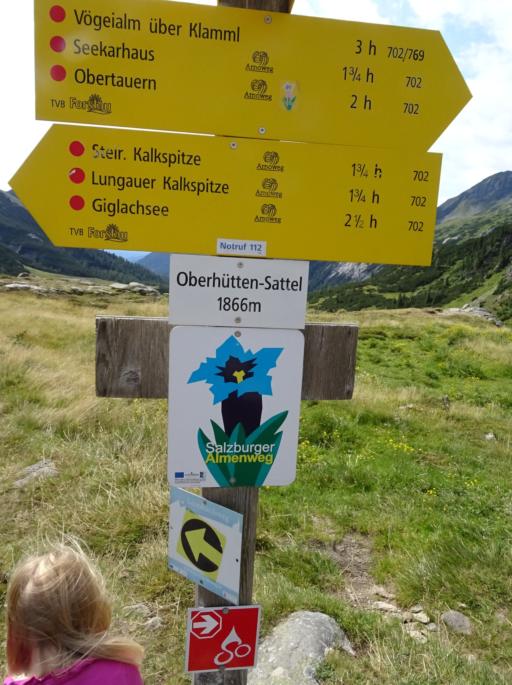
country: AT
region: Salzburg
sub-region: Politischer Bezirk Tamsweg
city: Tweng
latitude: 47.2769
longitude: 13.6015
